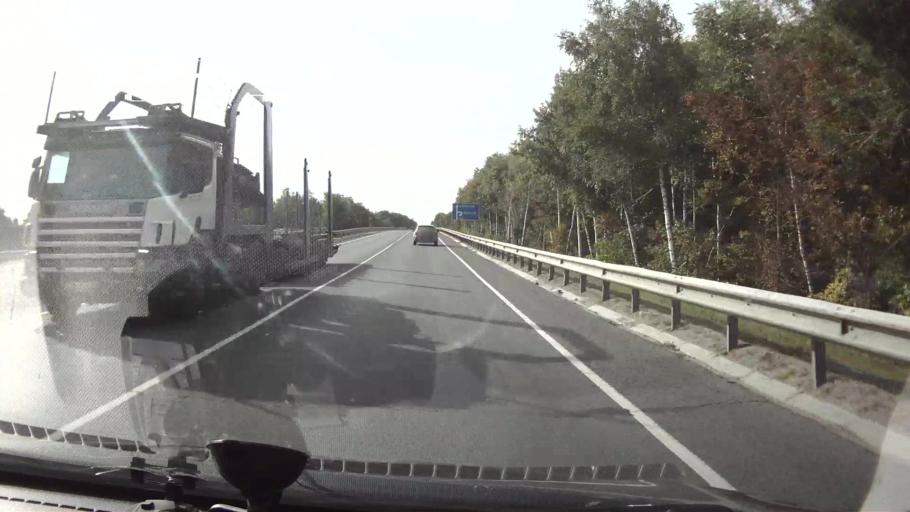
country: RU
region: Saratov
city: Vol'sk
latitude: 52.1092
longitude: 47.3843
